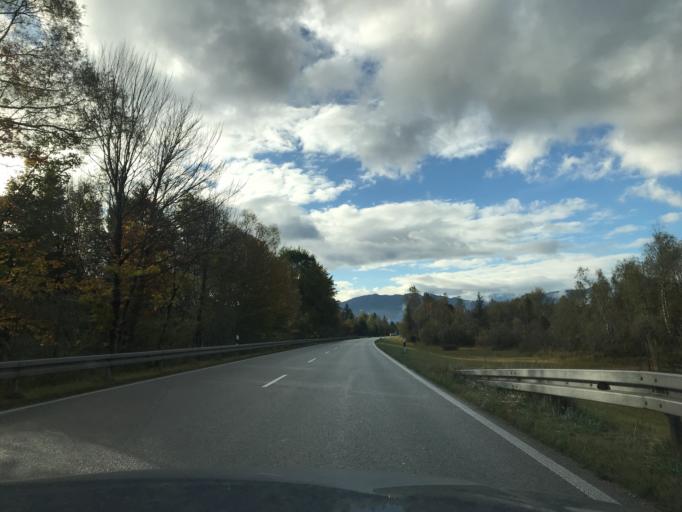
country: DE
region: Bavaria
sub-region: Upper Bavaria
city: Lenggries
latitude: 47.6974
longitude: 11.5633
